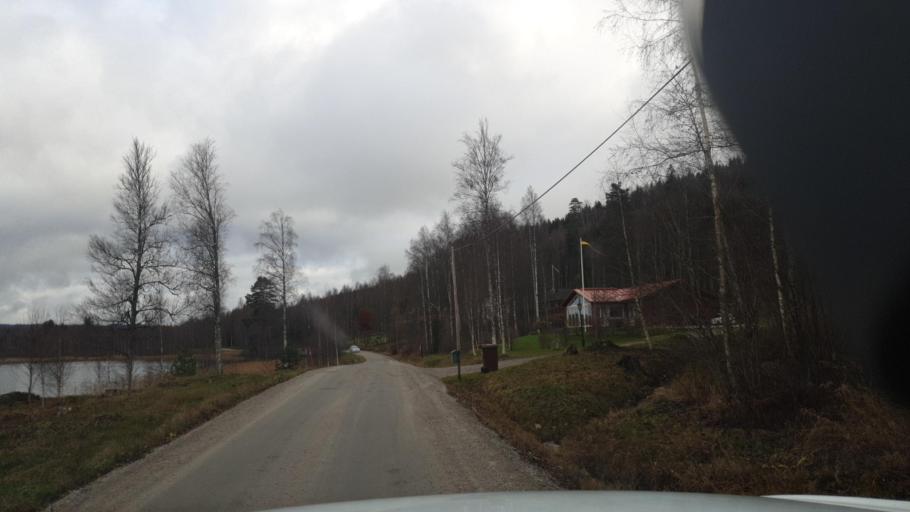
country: SE
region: Vaermland
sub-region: Arvika Kommun
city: Arvika
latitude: 59.7420
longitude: 12.8301
